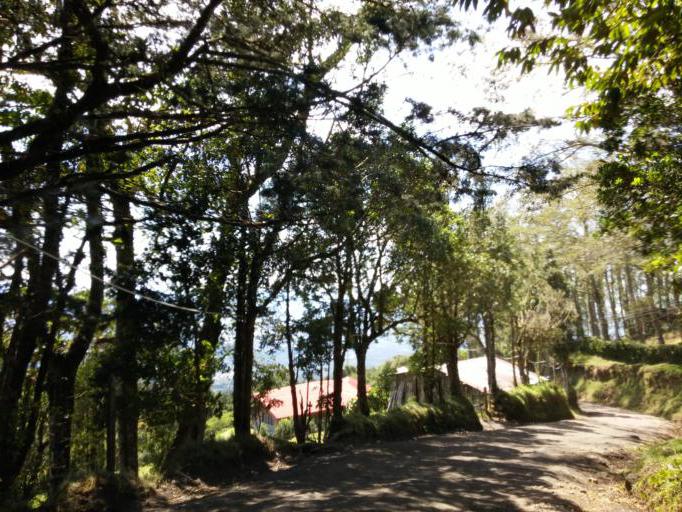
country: CR
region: Heredia
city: Santo Domingo
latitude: 10.1124
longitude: -84.1216
